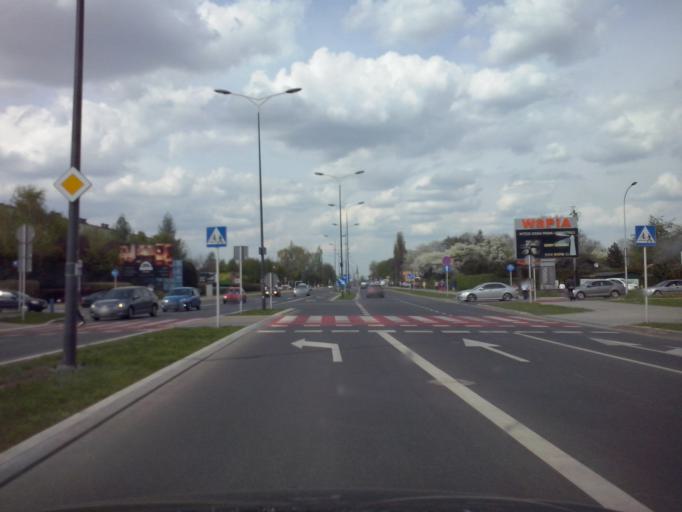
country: PL
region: Subcarpathian Voivodeship
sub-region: Rzeszow
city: Rzeszow
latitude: 50.0302
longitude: 22.0170
